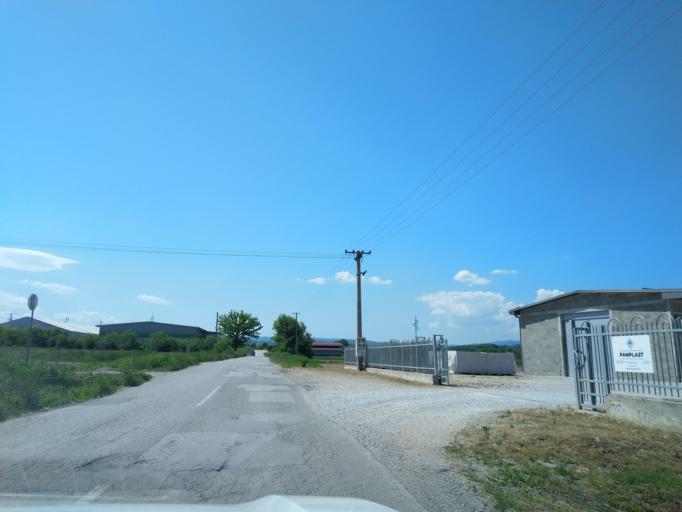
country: RS
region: Central Serbia
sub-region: Zlatiborski Okrug
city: Pozega
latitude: 43.8511
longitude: 20.0035
